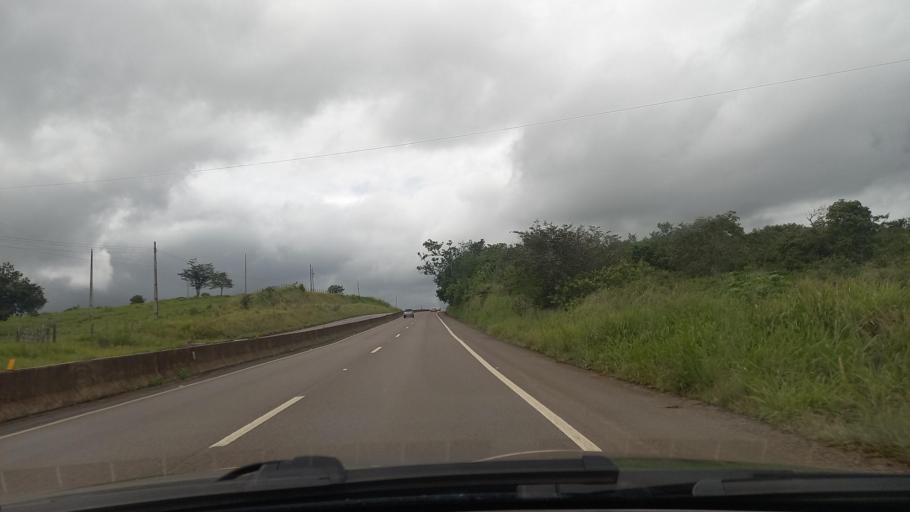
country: BR
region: Alagoas
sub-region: Limoeiro De Anadia
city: Limoeiro de Anadia
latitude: -9.7399
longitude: -36.4824
